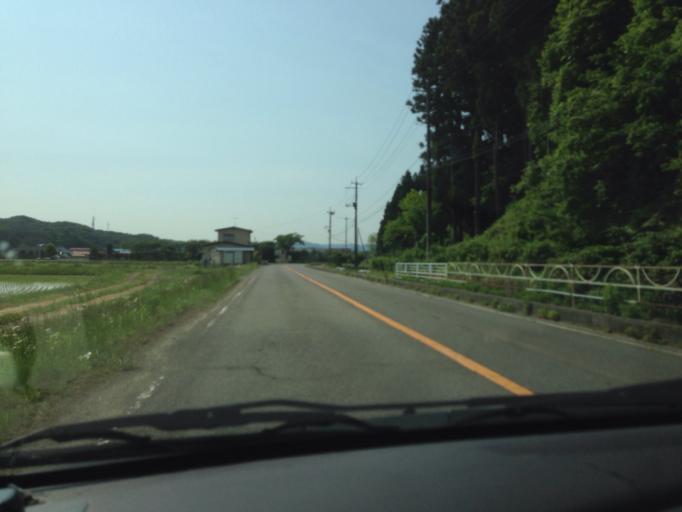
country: JP
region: Tochigi
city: Kuroiso
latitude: 37.1606
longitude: 140.1762
